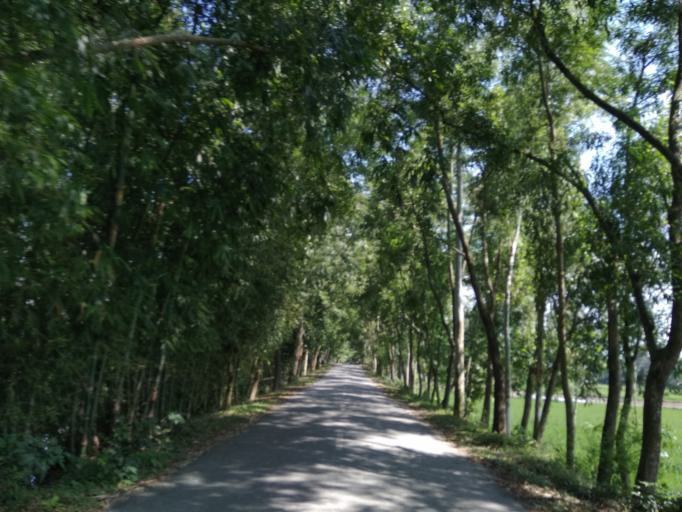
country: IN
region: West Bengal
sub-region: Koch Bihar
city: Haldibari
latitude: 26.1937
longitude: 88.6904
